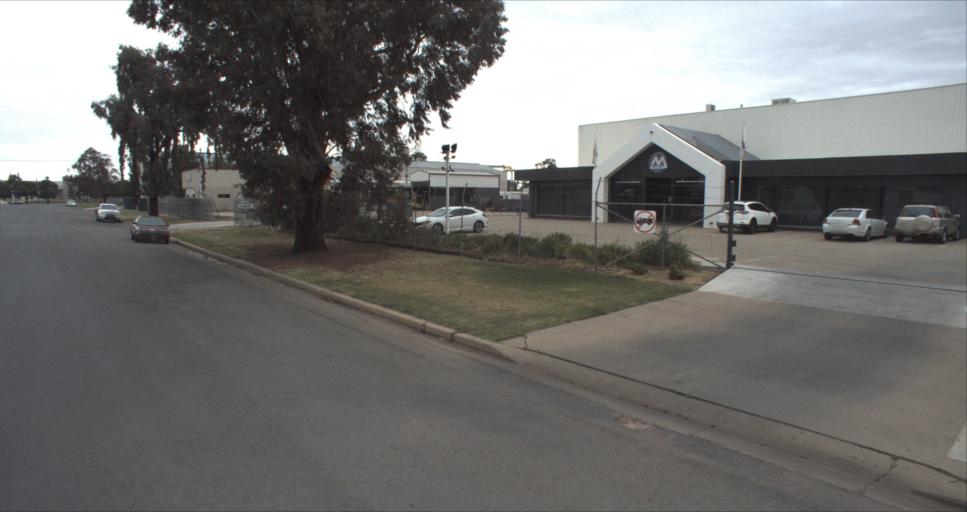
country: AU
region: New South Wales
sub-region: Leeton
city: Leeton
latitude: -34.5489
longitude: 146.3889
